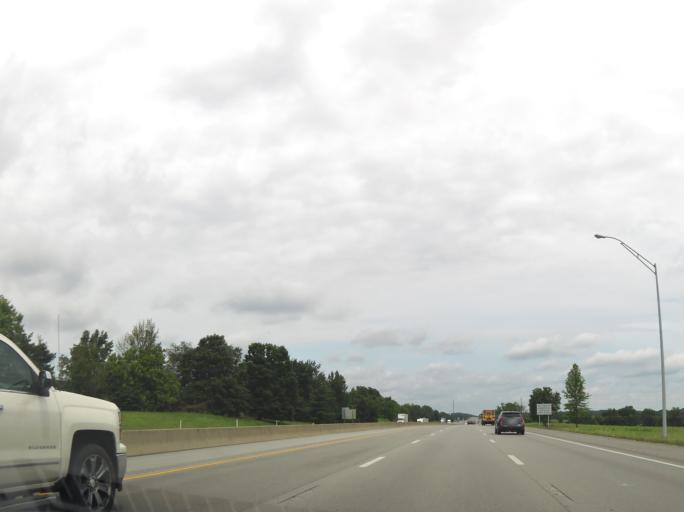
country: US
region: Kentucky
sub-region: Scott County
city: Georgetown
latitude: 38.2827
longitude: -84.5586
